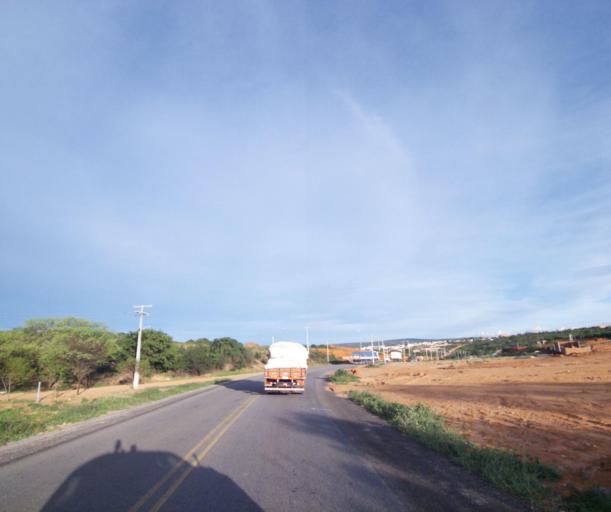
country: BR
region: Bahia
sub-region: Cacule
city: Cacule
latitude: -14.2025
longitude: -42.1264
